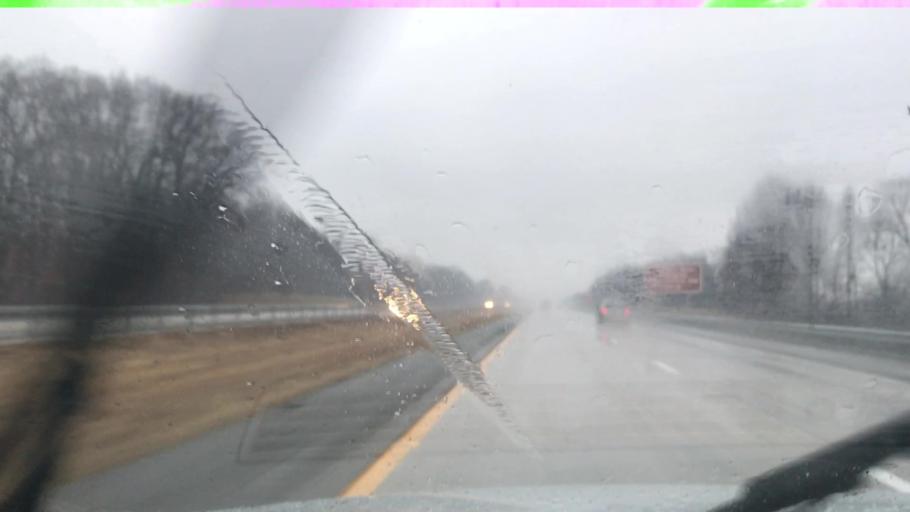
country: US
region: Kentucky
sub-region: Christian County
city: Oak Grove
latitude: 36.6624
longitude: -87.3765
